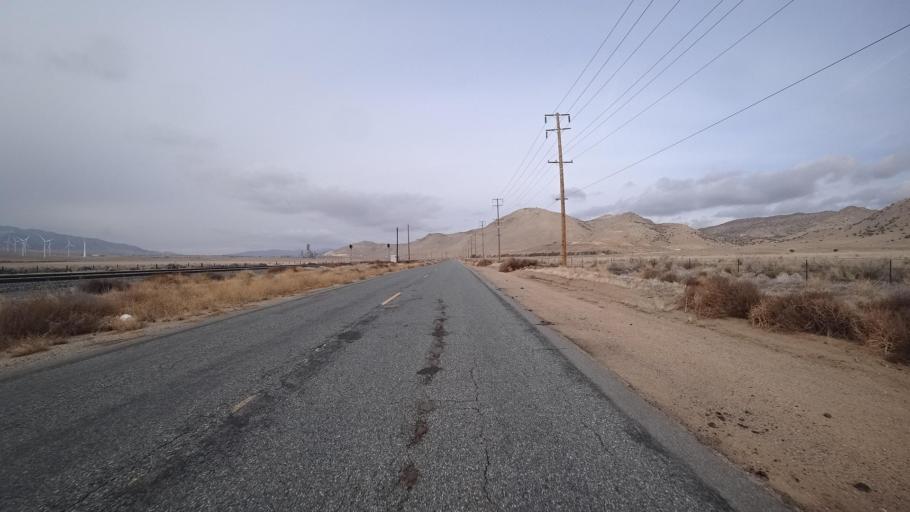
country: US
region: California
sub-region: Kern County
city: Tehachapi
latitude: 35.1169
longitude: -118.3353
